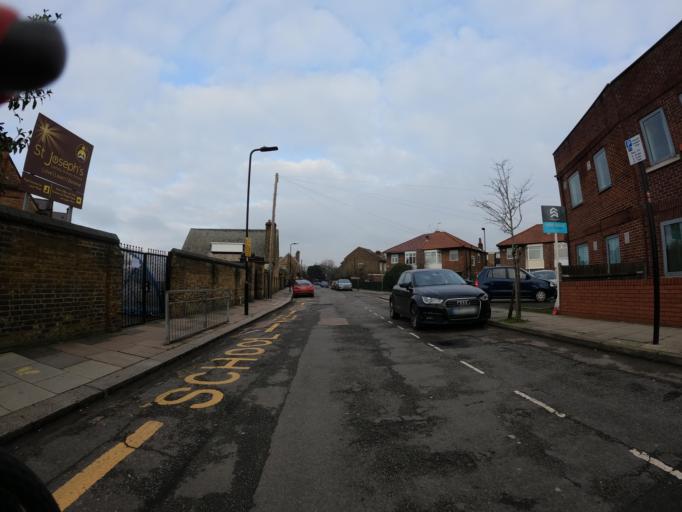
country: GB
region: England
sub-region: Greater London
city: Greenford
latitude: 51.5099
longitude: -0.3380
